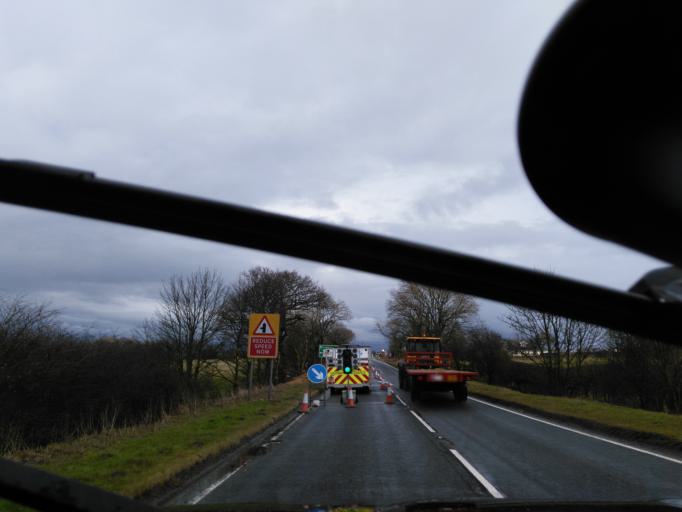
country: GB
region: England
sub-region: North Yorkshire
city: Stainburn
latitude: 54.0034
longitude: -1.6415
